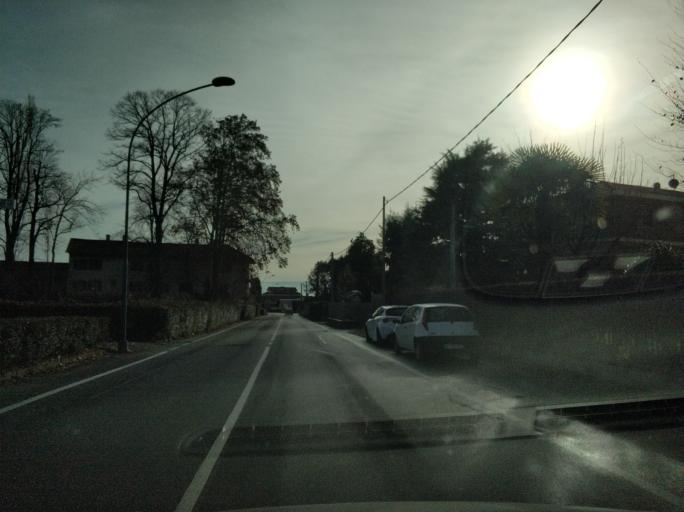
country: IT
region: Piedmont
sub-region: Provincia di Torino
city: Mathi
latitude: 45.2564
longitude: 7.5443
